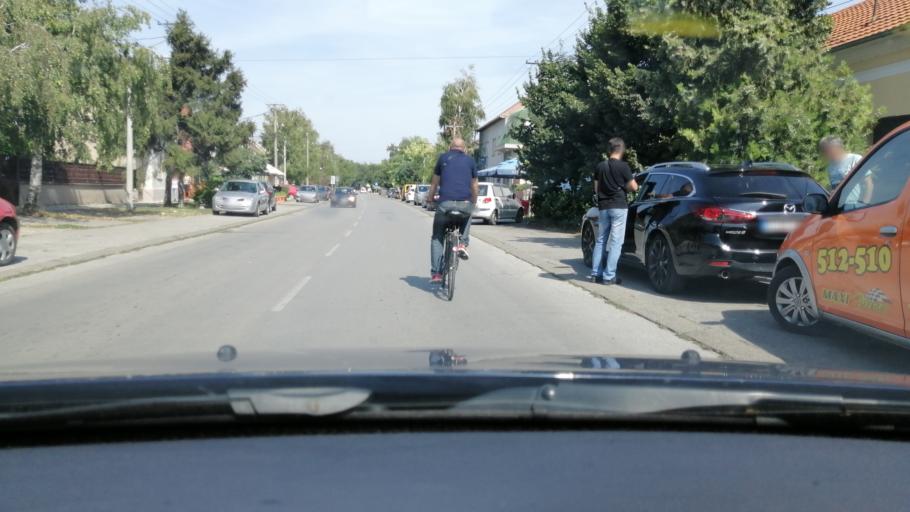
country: RS
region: Autonomna Pokrajina Vojvodina
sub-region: Srednjebanatski Okrug
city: Zrenjanin
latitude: 45.3847
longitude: 20.3877
